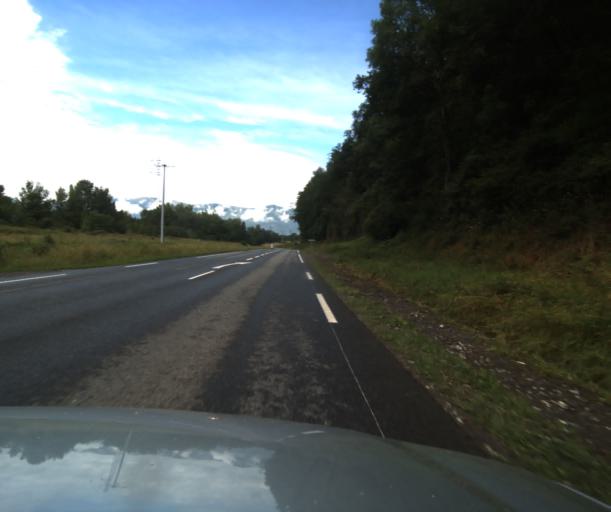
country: FR
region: Midi-Pyrenees
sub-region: Departement des Hautes-Pyrenees
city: Pierrefitte-Nestalas
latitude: 42.9679
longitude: -0.0616
